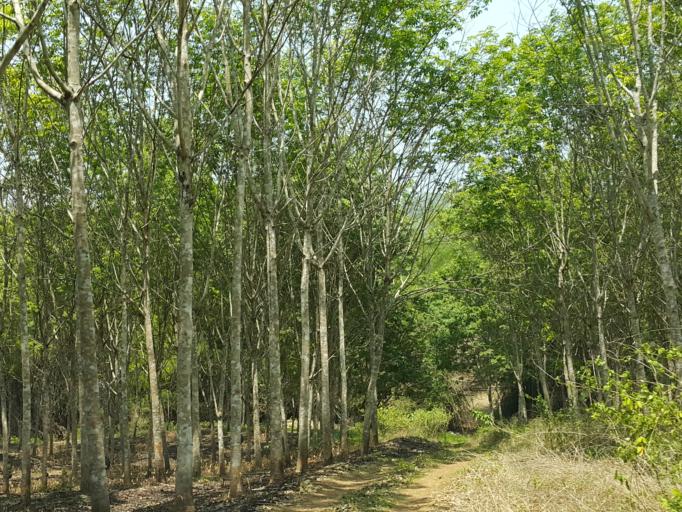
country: TH
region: Kanchanaburi
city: Sai Yok
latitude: 14.2140
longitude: 98.8769
